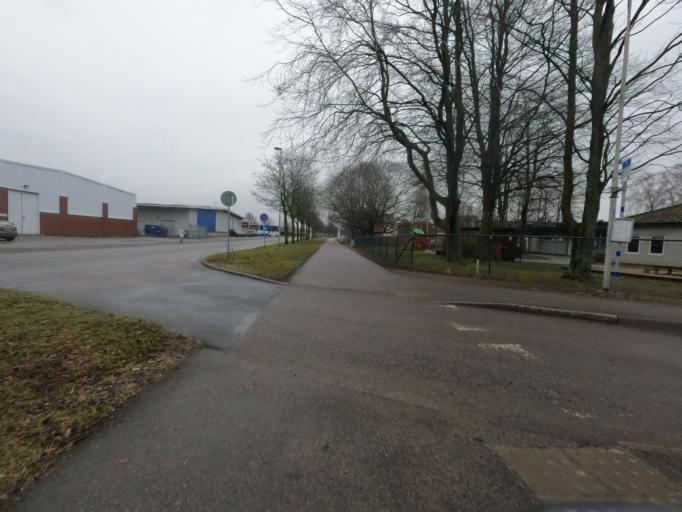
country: SE
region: Halland
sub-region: Halmstads Kommun
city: Halmstad
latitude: 56.6725
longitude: 12.8892
